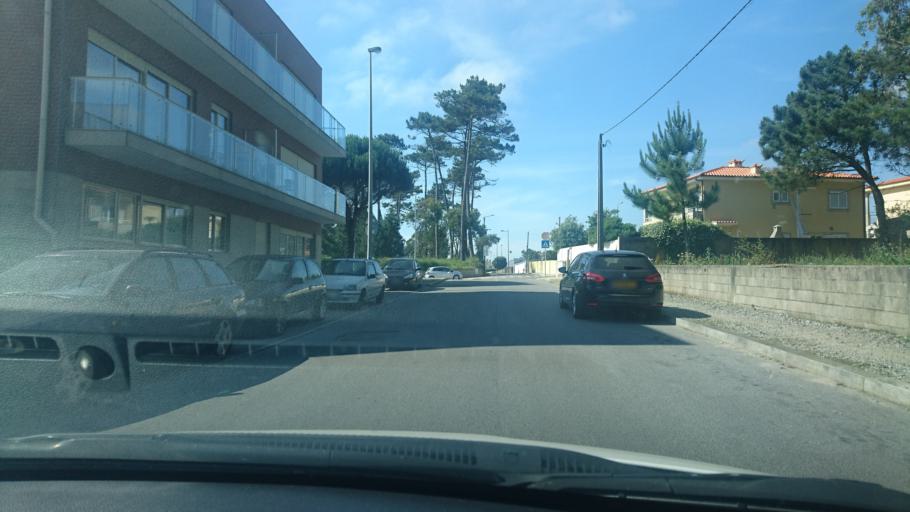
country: PT
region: Porto
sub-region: Matosinhos
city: Lavra
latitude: 41.2757
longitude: -8.7232
